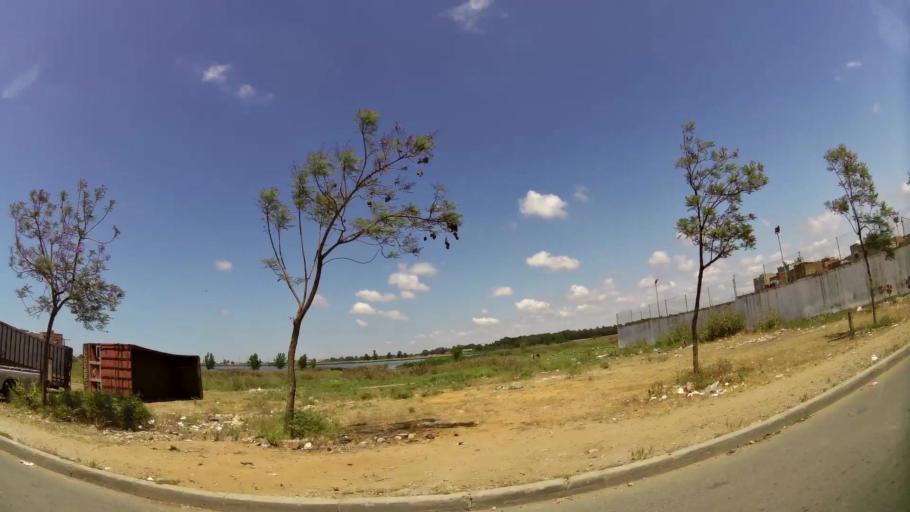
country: MA
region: Gharb-Chrarda-Beni Hssen
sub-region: Kenitra Province
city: Kenitra
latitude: 34.2585
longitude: -6.5496
